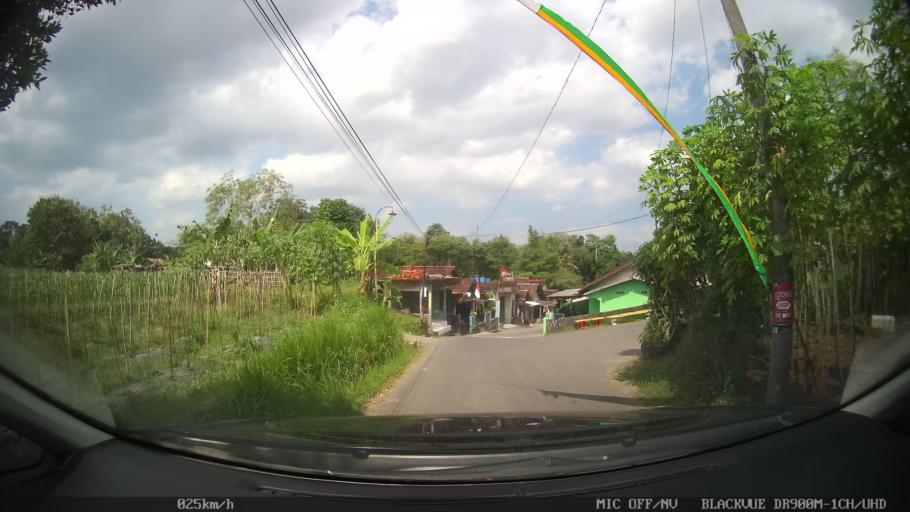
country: ID
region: Daerah Istimewa Yogyakarta
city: Yogyakarta
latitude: -7.7624
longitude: 110.3546
